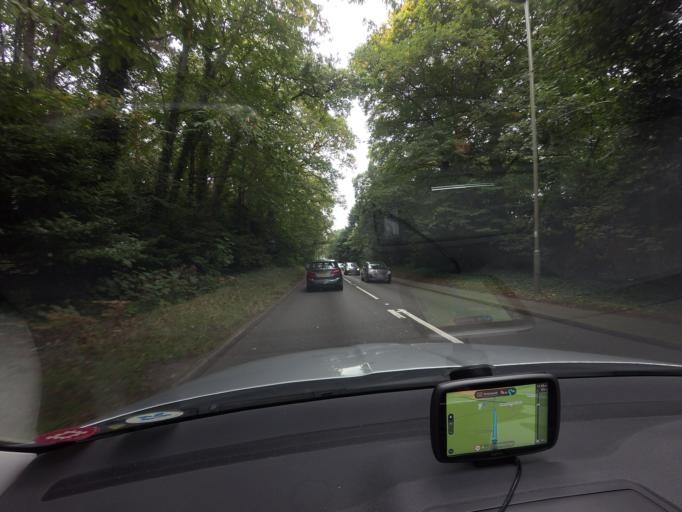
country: GB
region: England
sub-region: Surrey
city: Byfleet
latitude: 51.3369
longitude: -0.4417
